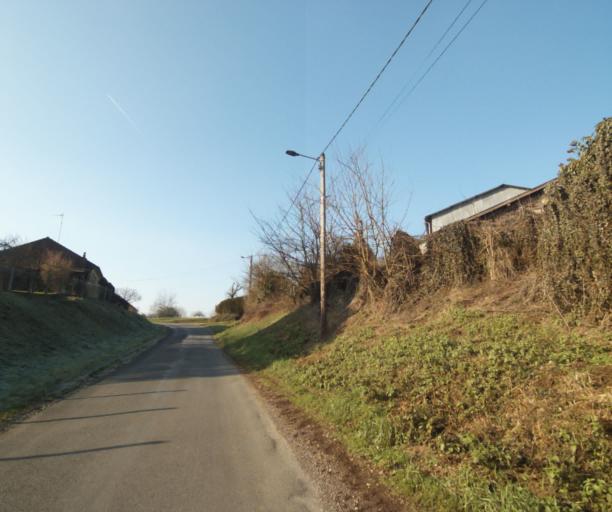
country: FR
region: Champagne-Ardenne
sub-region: Departement de la Haute-Marne
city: Laneuville-a-Remy
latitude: 48.4608
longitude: 4.9195
